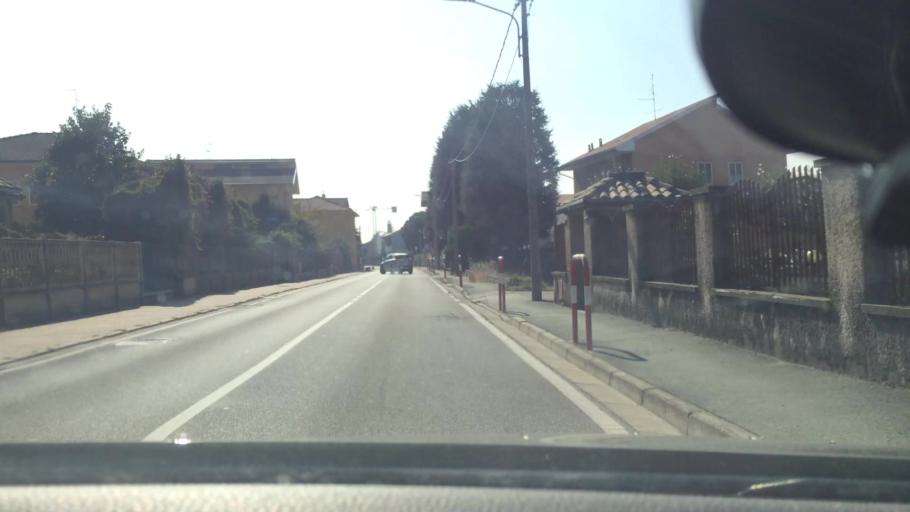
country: IT
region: Lombardy
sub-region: Provincia di Varese
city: Uboldo
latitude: 45.6193
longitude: 9.0029
